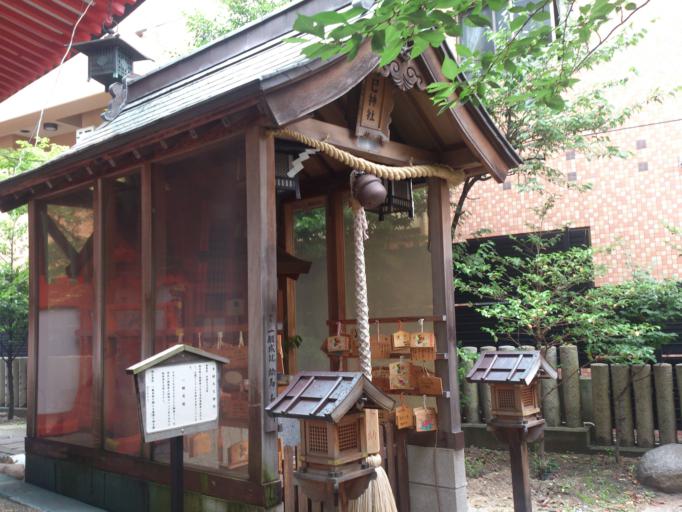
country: JP
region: Hyogo
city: Kobe
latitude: 34.6910
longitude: 135.1822
